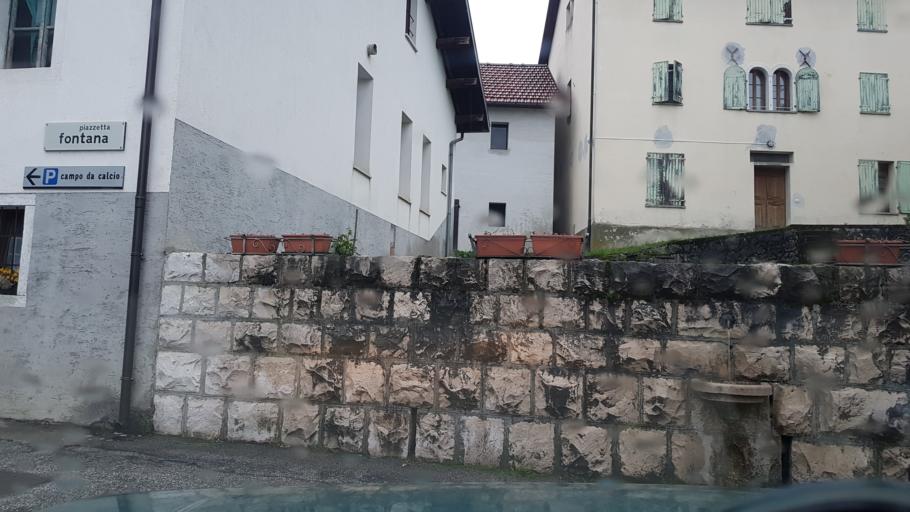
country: IT
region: Veneto
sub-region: Provincia di Belluno
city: Lamosano
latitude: 46.1658
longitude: 12.3923
